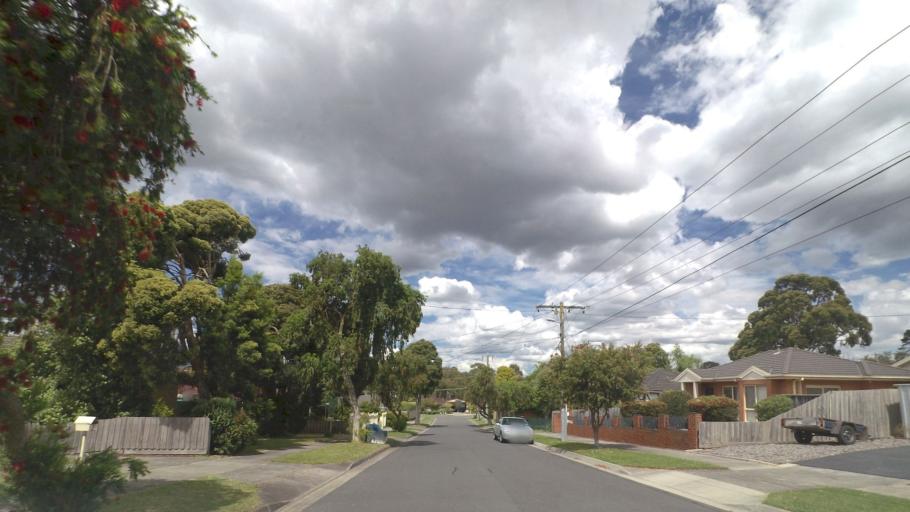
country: AU
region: Victoria
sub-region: Knox
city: Wantirna
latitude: -37.8486
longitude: 145.2348
